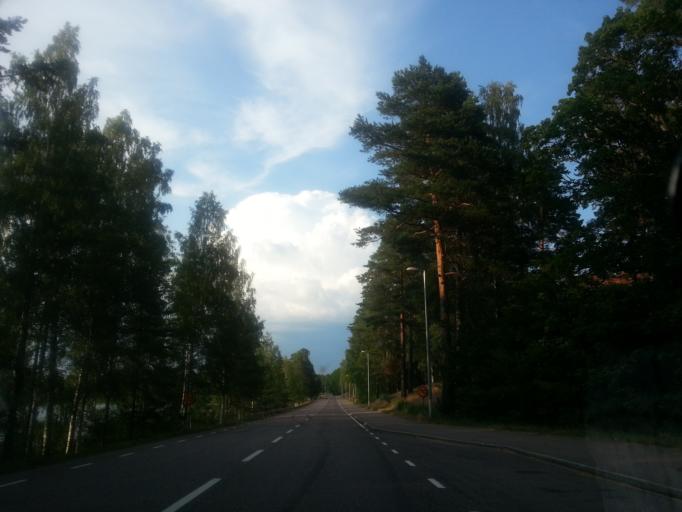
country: SE
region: Dalarna
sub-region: Avesta Kommun
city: Horndal
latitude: 60.2965
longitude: 16.4087
